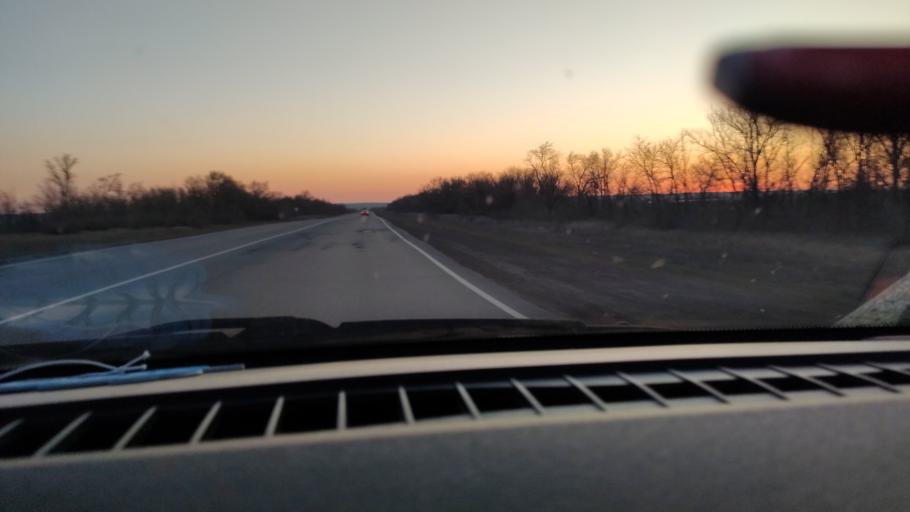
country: RU
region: Saratov
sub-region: Saratovskiy Rayon
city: Saratov
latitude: 51.7087
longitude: 46.0162
